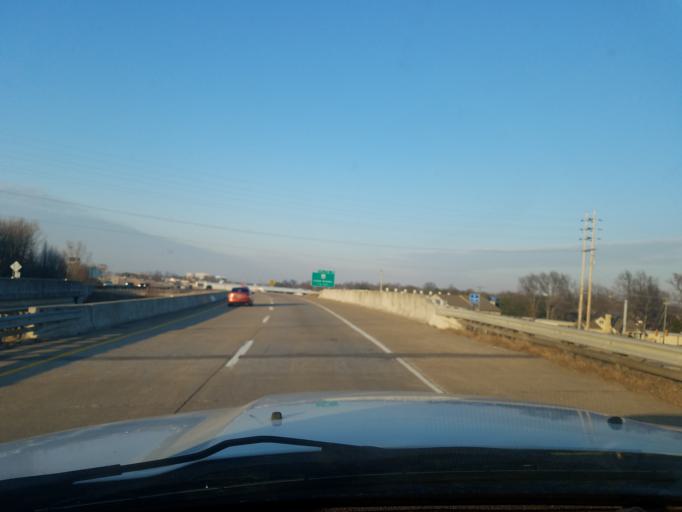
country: US
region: Indiana
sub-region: Warrick County
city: Newburgh
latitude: 37.9546
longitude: -87.4485
